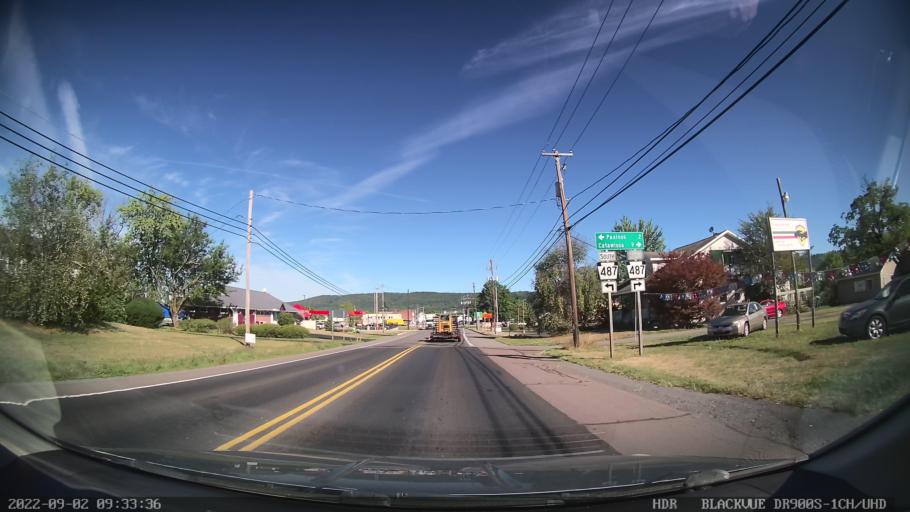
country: US
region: Pennsylvania
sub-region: Northumberland County
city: Elysburg
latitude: 40.8599
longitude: -76.5475
